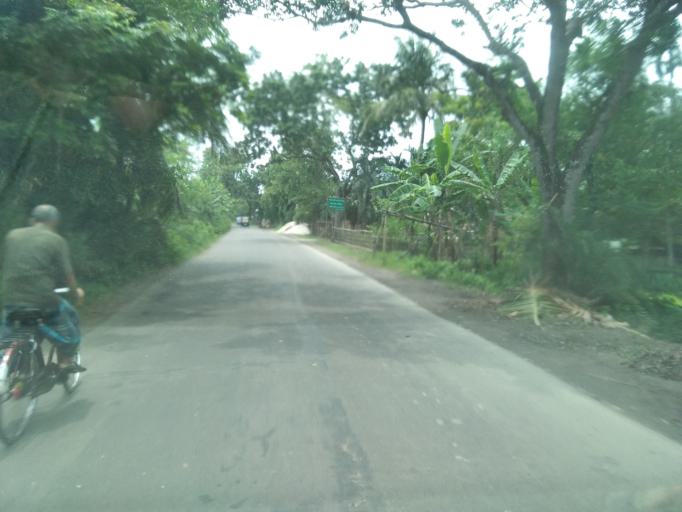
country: IN
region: West Bengal
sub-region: North 24 Parganas
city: Taki
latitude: 22.5777
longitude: 88.9985
